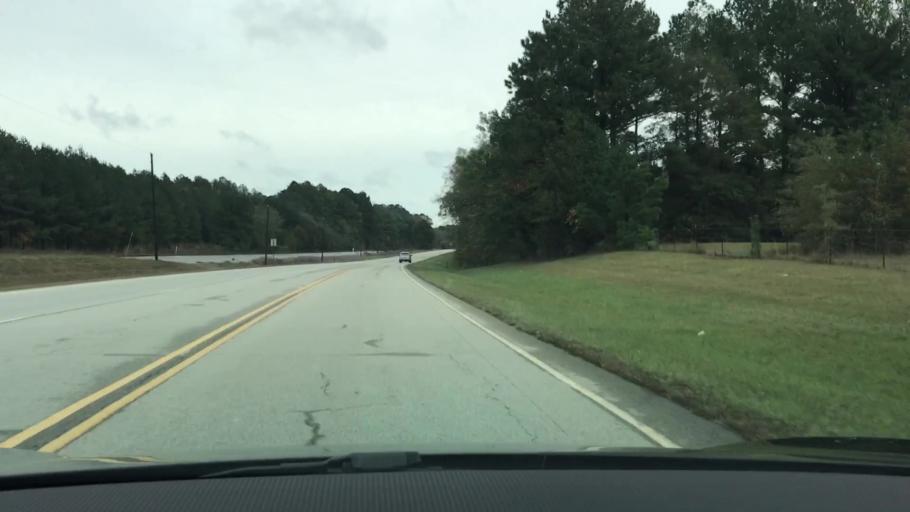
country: US
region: Georgia
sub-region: Warren County
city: Firing Range
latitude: 33.4777
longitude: -82.7339
